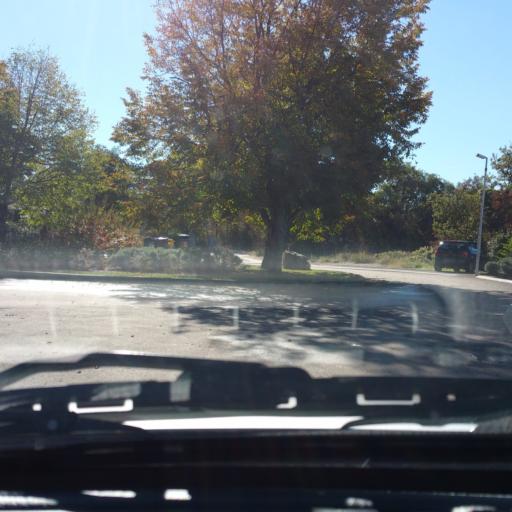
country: HR
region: Primorsko-Goranska
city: Njivice
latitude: 45.1493
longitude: 14.5406
